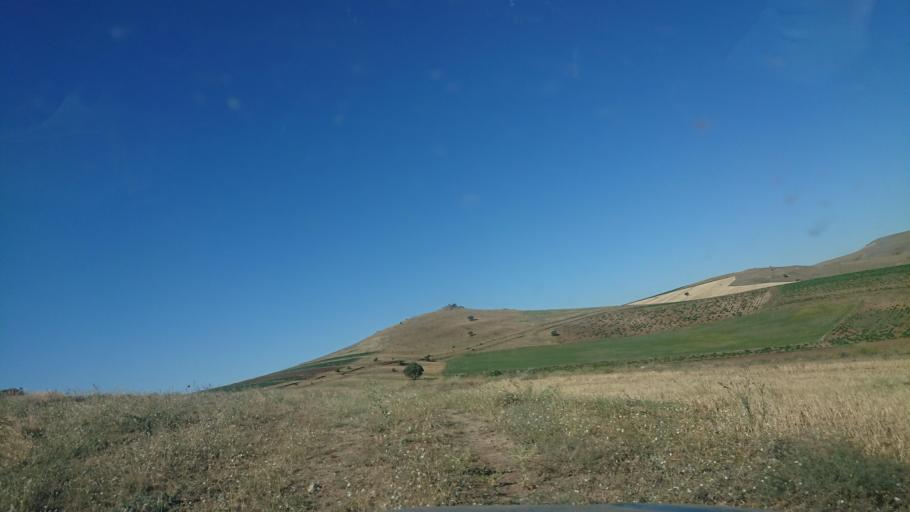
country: TR
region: Aksaray
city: Agacoren
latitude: 38.8385
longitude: 33.9364
